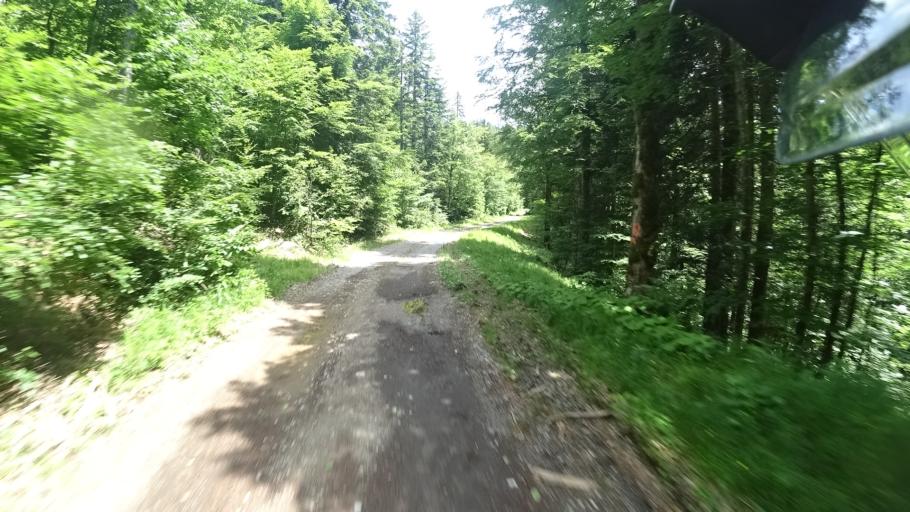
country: SI
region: Osilnica
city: Osilnica
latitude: 45.5399
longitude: 14.5887
